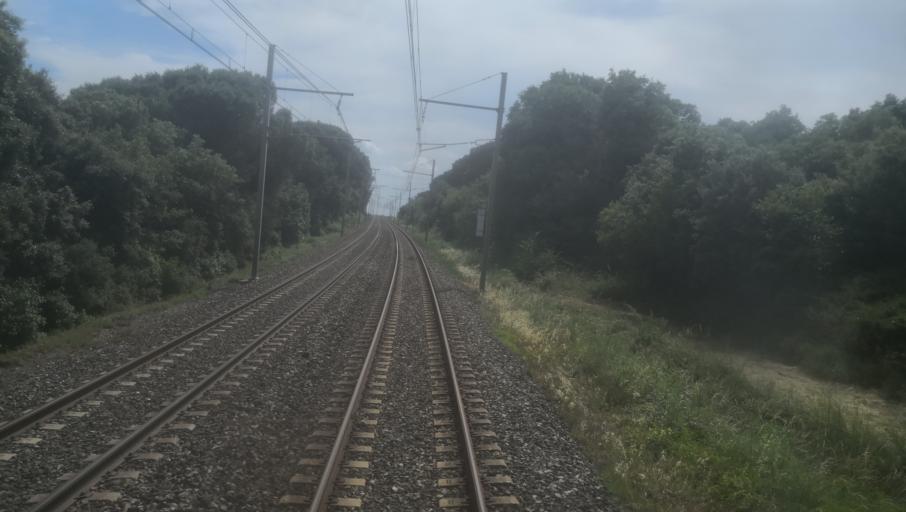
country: FR
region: Languedoc-Roussillon
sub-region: Departement du Gard
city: Jonquieres-Saint-Vincent
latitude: 43.7941
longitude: 4.5614
